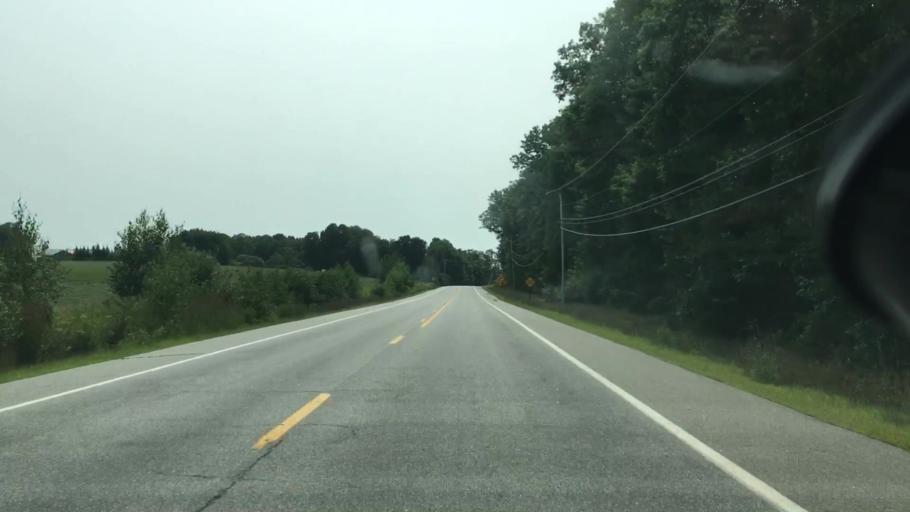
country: US
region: Maine
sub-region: Androscoggin County
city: Livermore Falls
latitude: 44.4260
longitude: -70.1452
